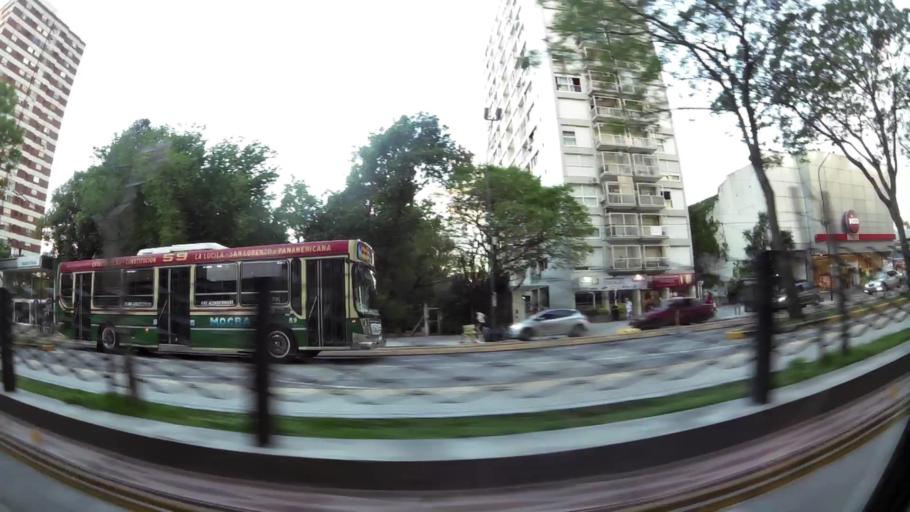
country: AR
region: Buenos Aires
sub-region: Partido de Vicente Lopez
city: Olivos
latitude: -34.5203
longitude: -58.4858
